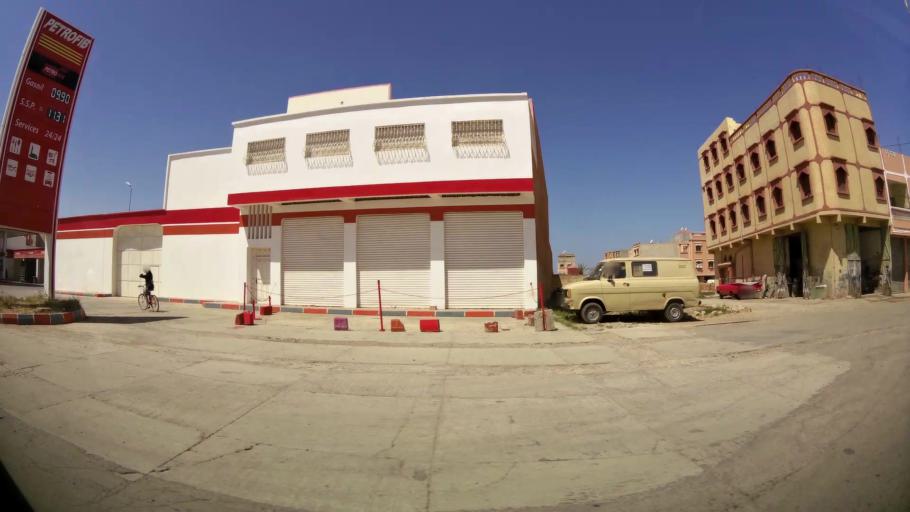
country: MA
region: Souss-Massa-Draa
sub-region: Inezgane-Ait Mellou
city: Inezgane
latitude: 30.3151
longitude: -9.5030
